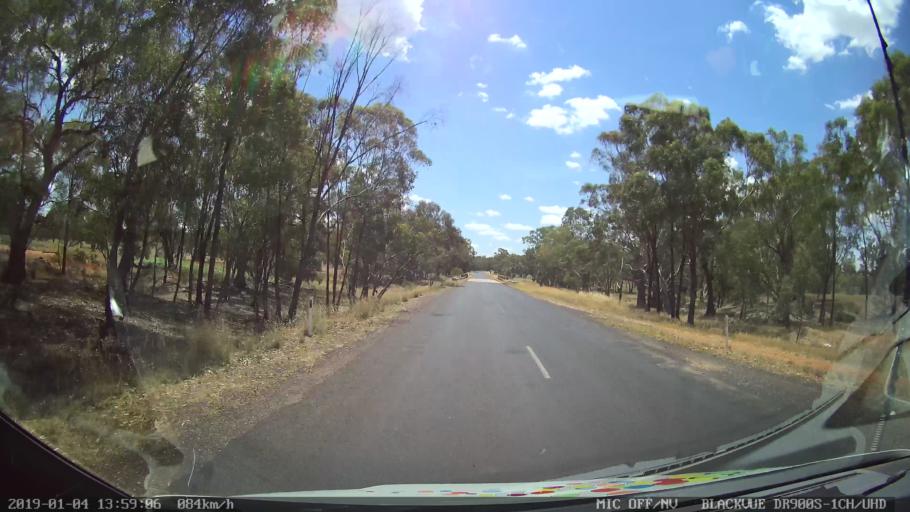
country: AU
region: New South Wales
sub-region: Dubbo Municipality
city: Dubbo
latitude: -32.3210
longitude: 148.5915
